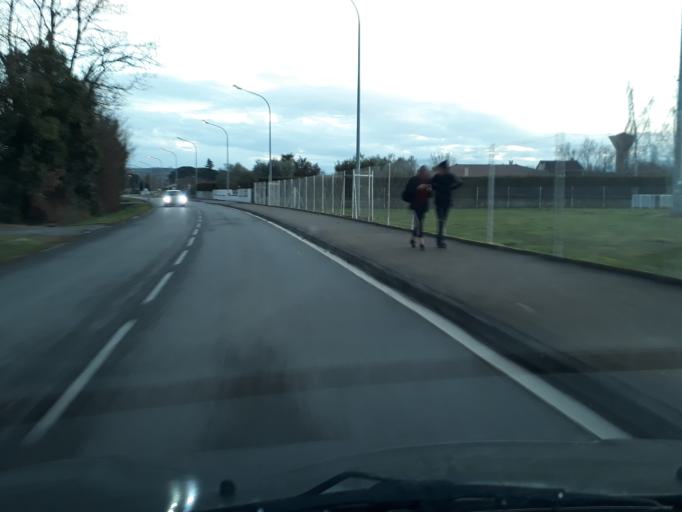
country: FR
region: Midi-Pyrenees
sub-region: Departement de la Haute-Garonne
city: Carbonne
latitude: 43.3082
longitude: 1.2294
